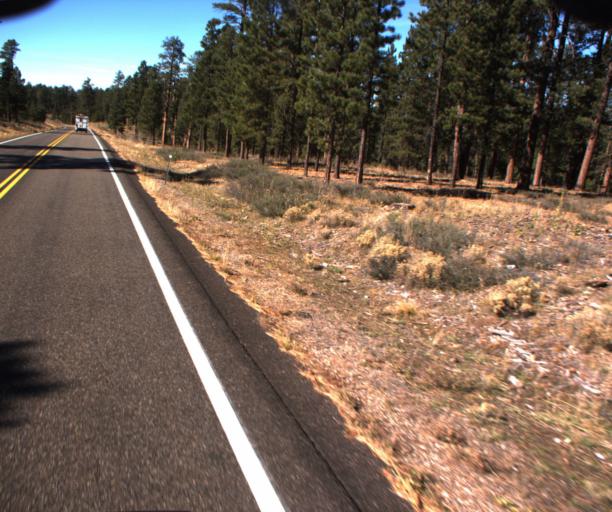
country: US
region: Arizona
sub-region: Coconino County
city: Fredonia
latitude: 36.6681
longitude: -112.2010
